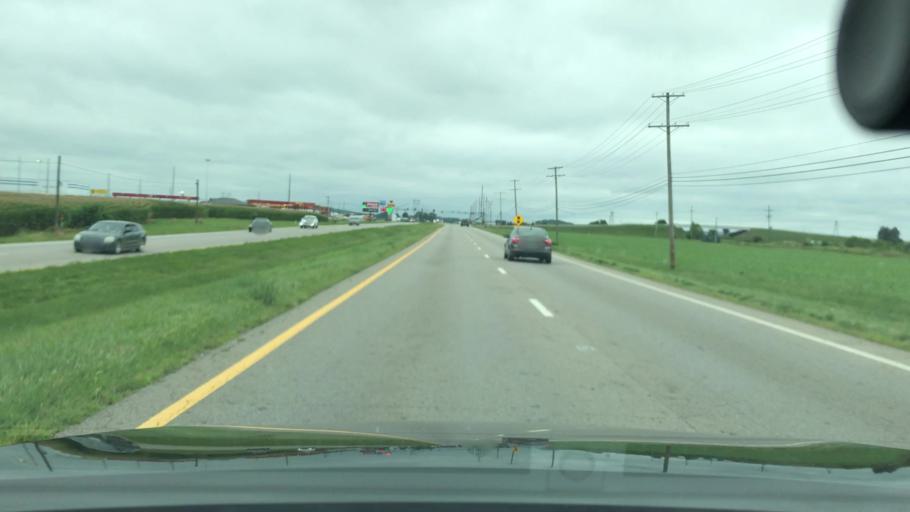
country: US
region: Ohio
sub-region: Pickaway County
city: Logan Elm Village
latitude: 39.5615
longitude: -82.9572
